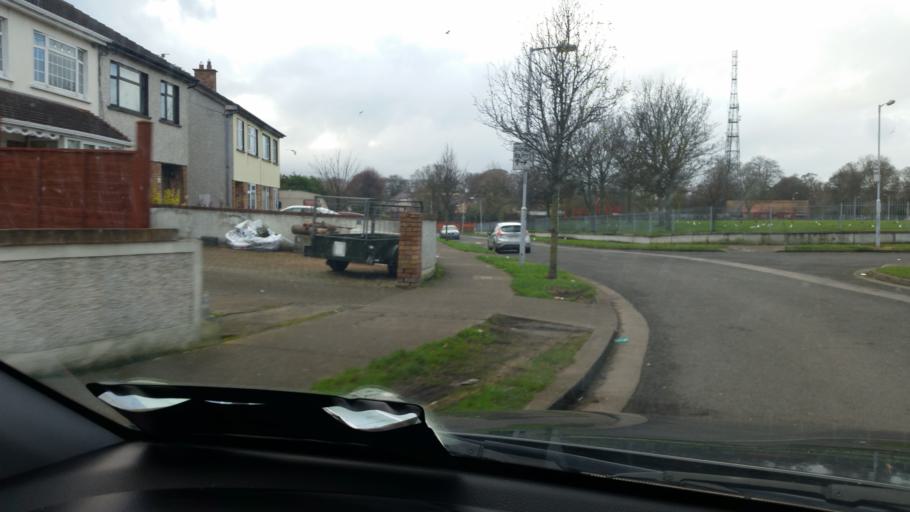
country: IE
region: Leinster
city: Cabra
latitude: 53.3593
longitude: -6.2998
